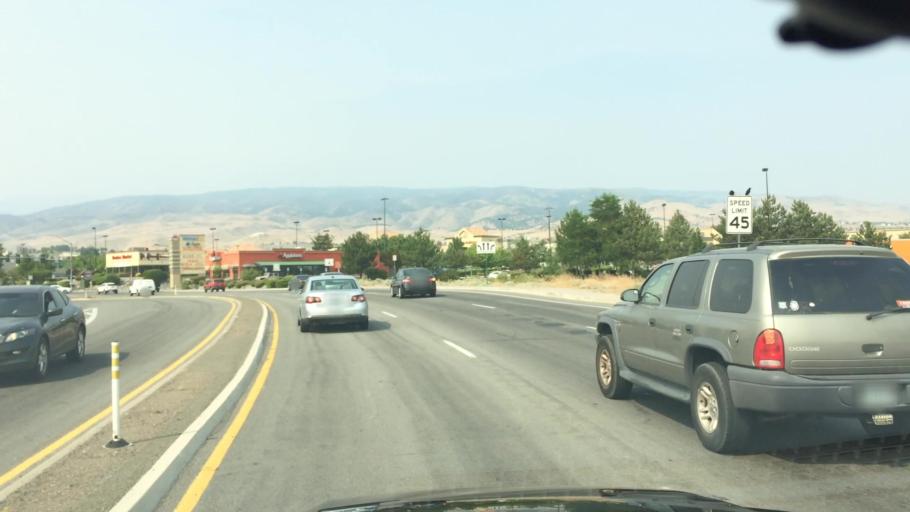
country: US
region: Nevada
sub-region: Washoe County
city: Reno
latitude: 39.4820
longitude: -119.7922
